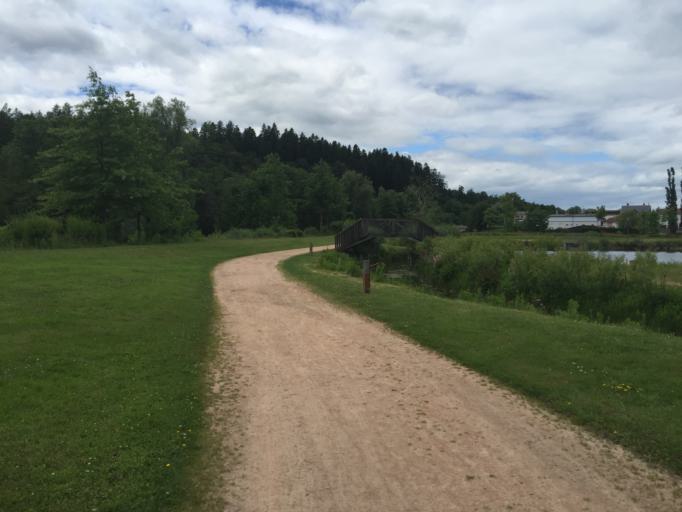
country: FR
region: Auvergne
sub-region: Departement du Puy-de-Dome
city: Ambert
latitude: 45.5480
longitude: 3.7323
